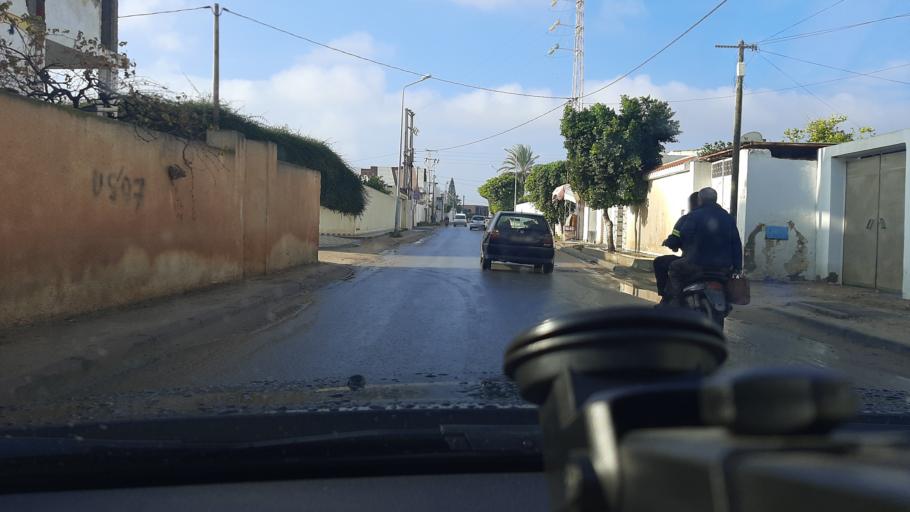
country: TN
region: Safaqis
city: Sfax
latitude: 34.7447
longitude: 10.7194
